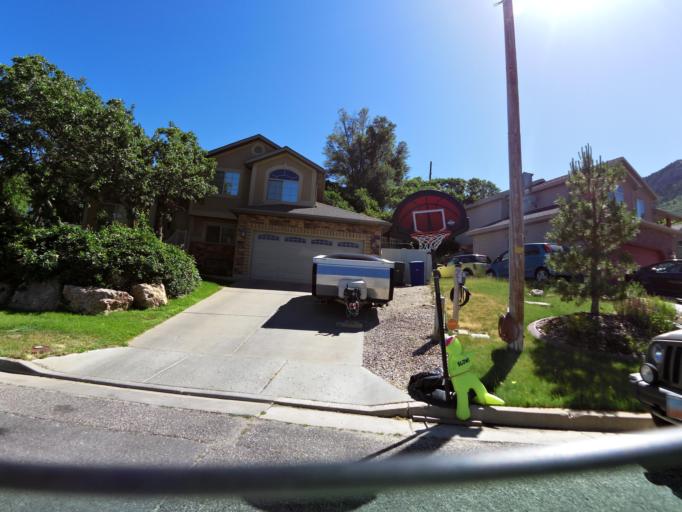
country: US
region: Utah
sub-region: Weber County
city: Ogden
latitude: 41.2317
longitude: -111.9348
